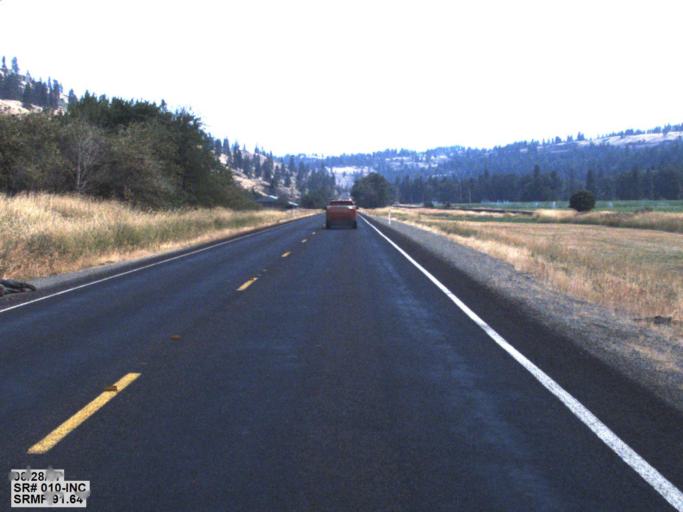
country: US
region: Washington
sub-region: Kittitas County
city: Cle Elum
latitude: 47.1493
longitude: -120.8023
